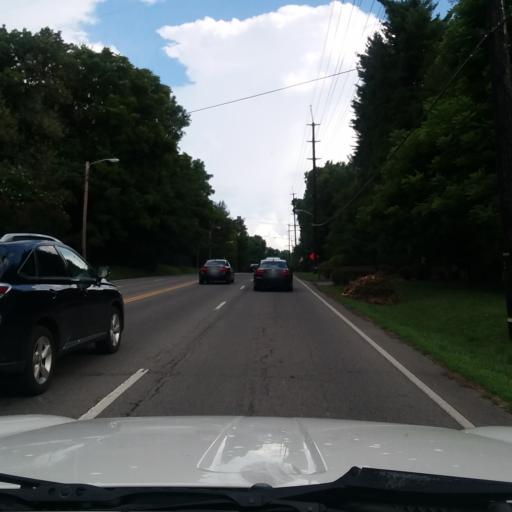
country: US
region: Tennessee
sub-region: Davidson County
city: Oak Hill
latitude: 36.0943
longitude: -86.7717
